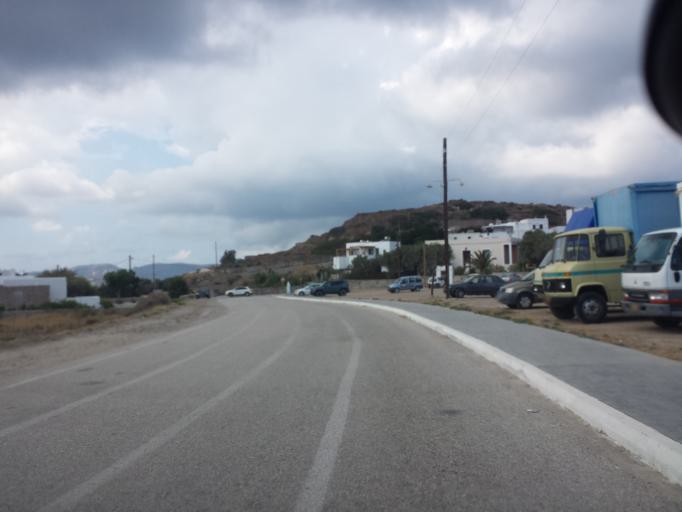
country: GR
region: South Aegean
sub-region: Nomos Kykladon
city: Milos
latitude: 36.7433
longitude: 24.4248
